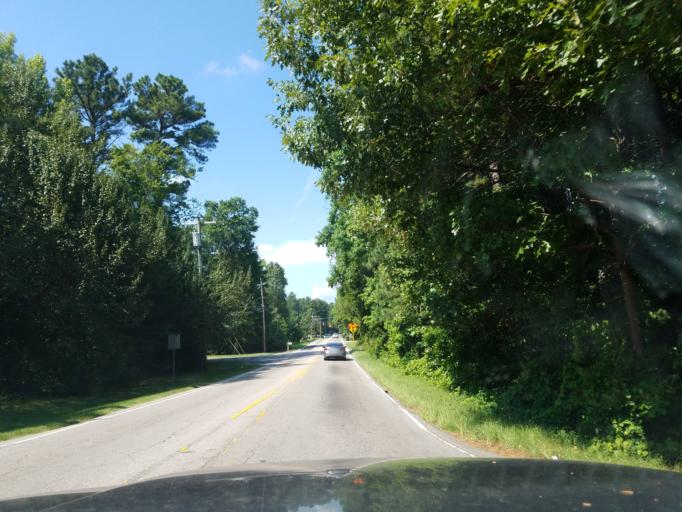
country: US
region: North Carolina
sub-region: Durham County
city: Durham
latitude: 35.9308
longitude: -78.9181
